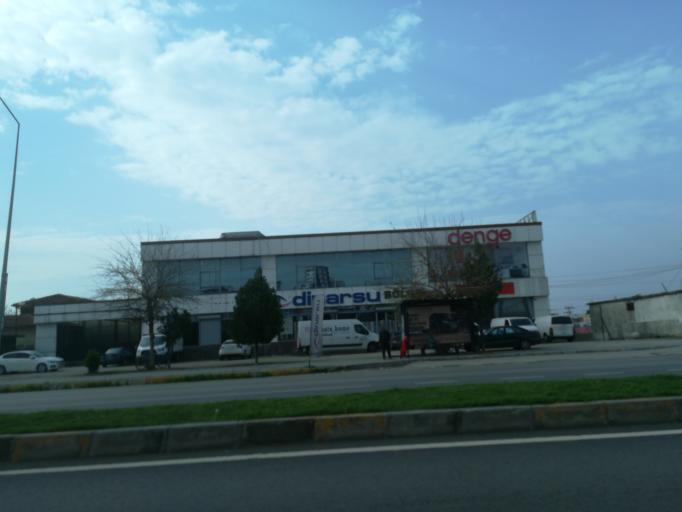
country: TR
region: Adana
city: Yuregir
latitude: 36.9855
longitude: 35.3663
